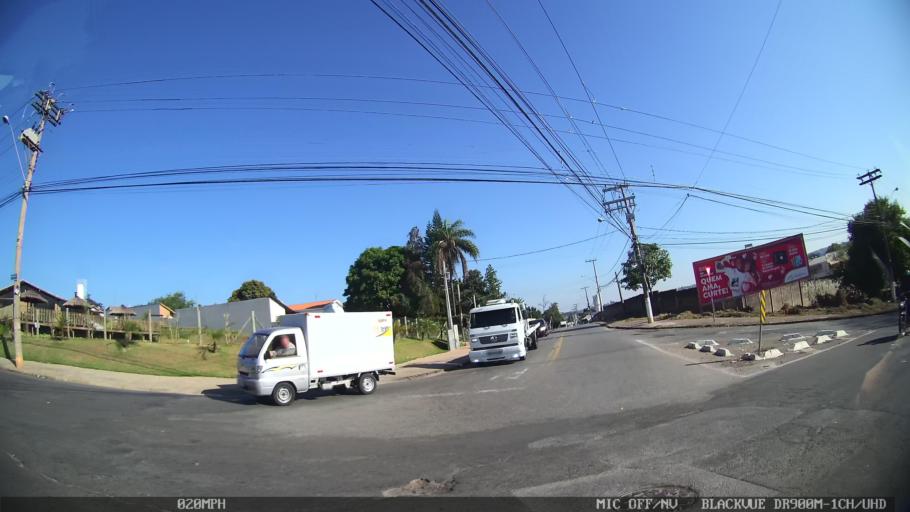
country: BR
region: Sao Paulo
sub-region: Campinas
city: Campinas
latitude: -22.9643
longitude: -47.1079
